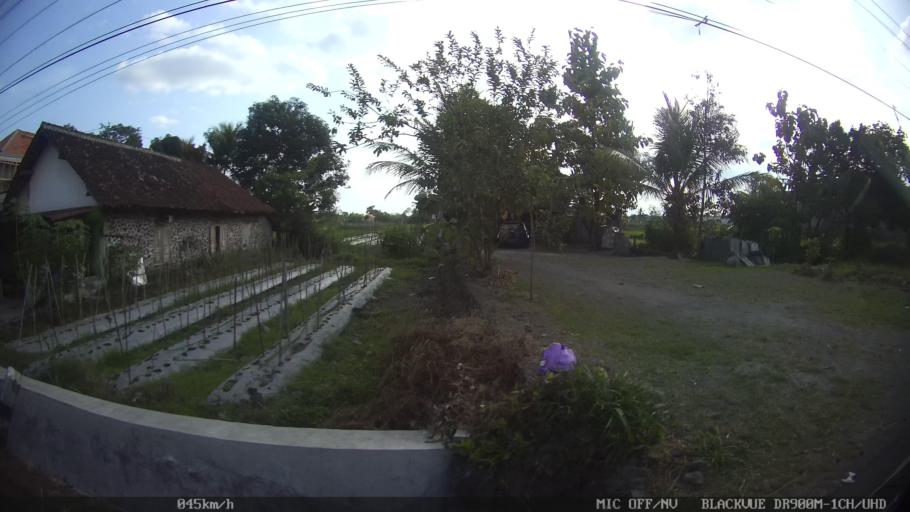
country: ID
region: Central Java
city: Candi Prambanan
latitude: -7.7055
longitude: 110.4678
